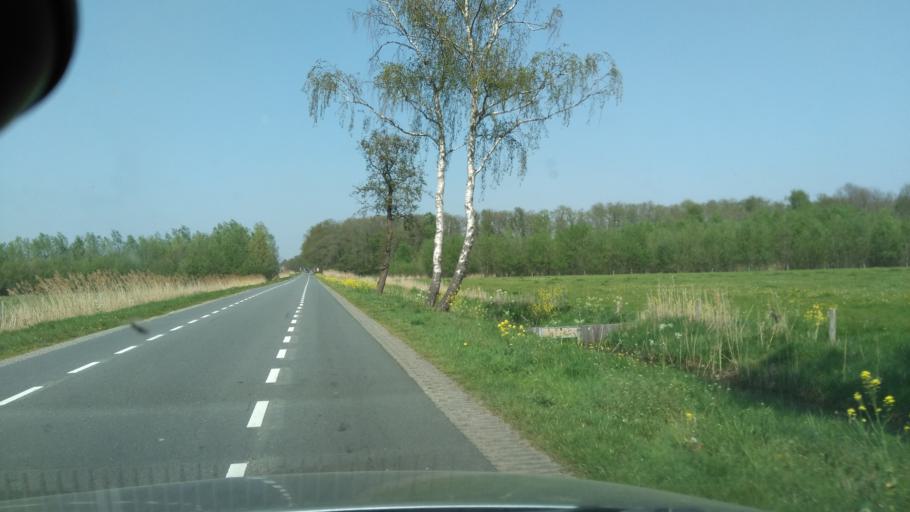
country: NL
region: North Brabant
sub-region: Gemeente Baarle-Nassau
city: Baarle-Nassau
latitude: 51.4779
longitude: 4.8604
